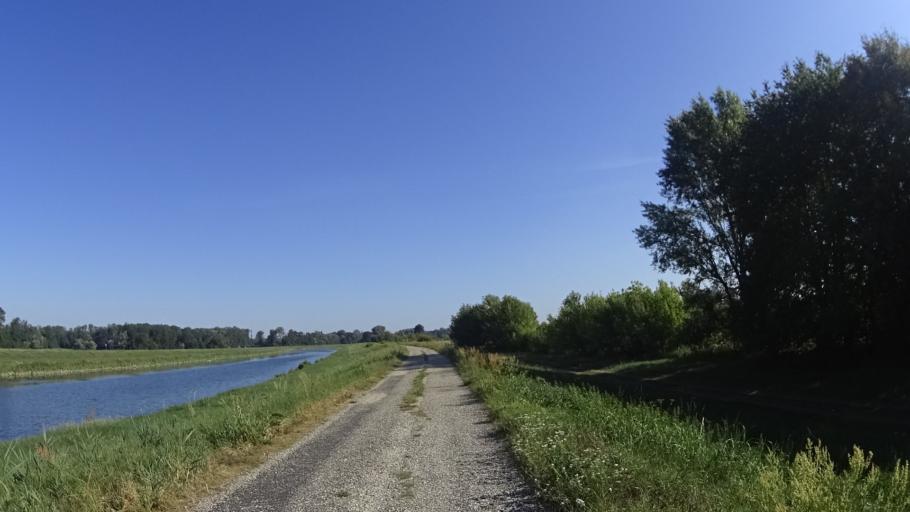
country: CZ
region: South Moravian
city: Kostice
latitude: 48.7201
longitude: 17.0141
